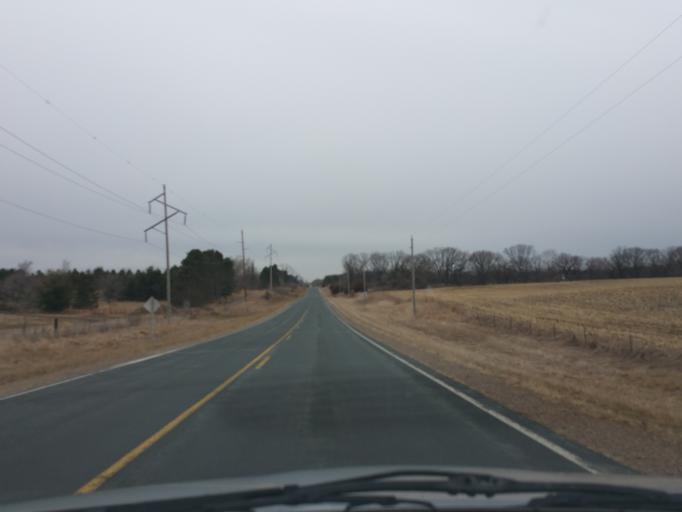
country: US
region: Wisconsin
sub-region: Saint Croix County
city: Roberts
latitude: 45.0357
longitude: -92.6113
